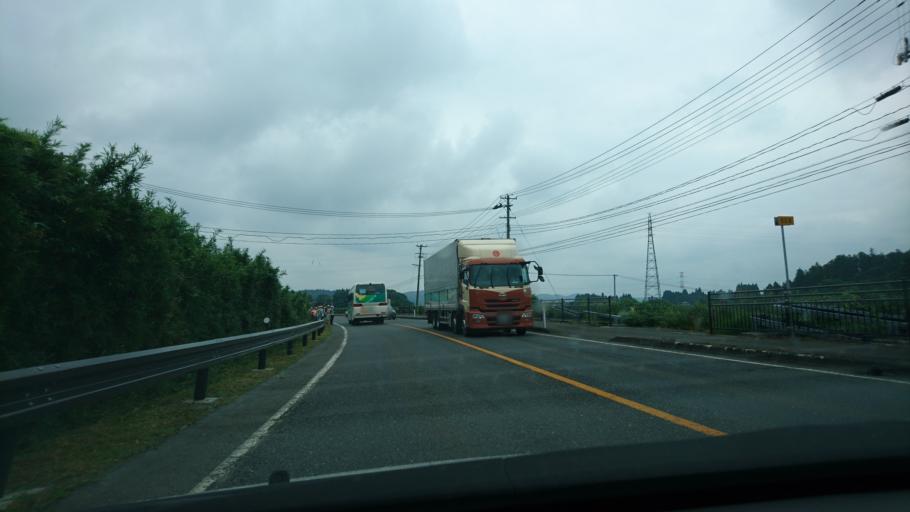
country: JP
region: Miyagi
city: Furukawa
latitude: 38.7161
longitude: 140.8087
